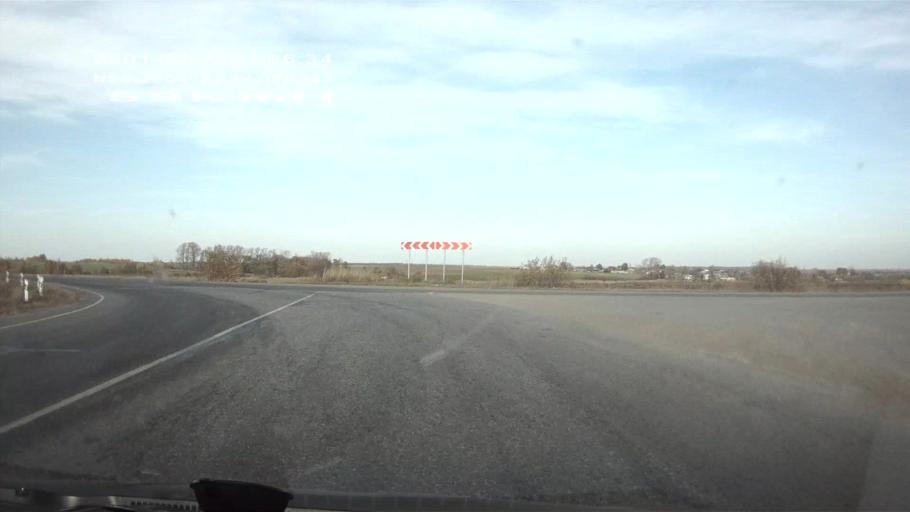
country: RU
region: Chuvashia
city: Ibresi
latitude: 55.2855
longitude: 47.0803
